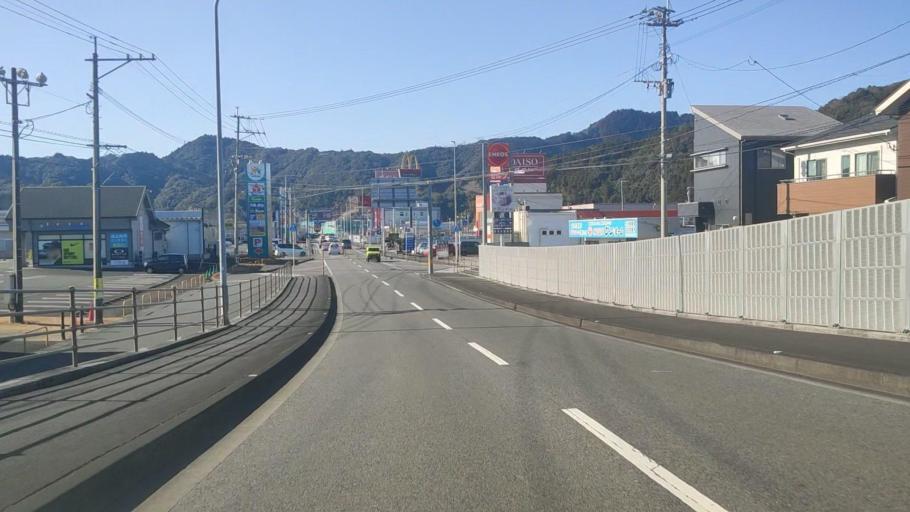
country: JP
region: Oita
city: Saiki
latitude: 32.9610
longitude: 131.8694
